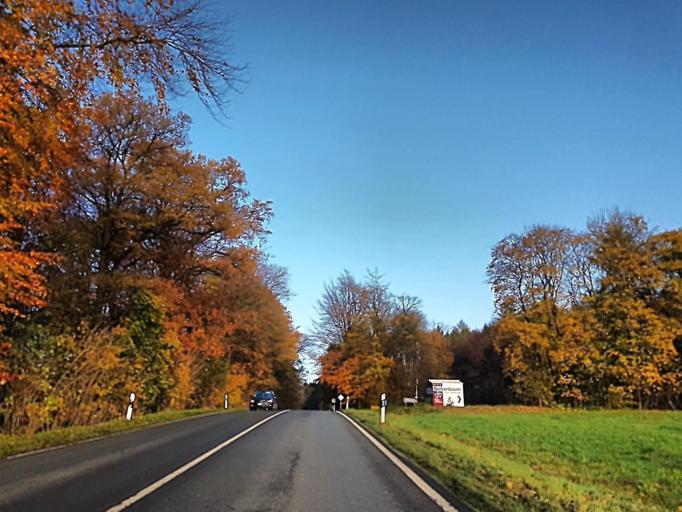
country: DE
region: North Rhine-Westphalia
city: Kierspe
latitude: 51.1482
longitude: 7.5781
